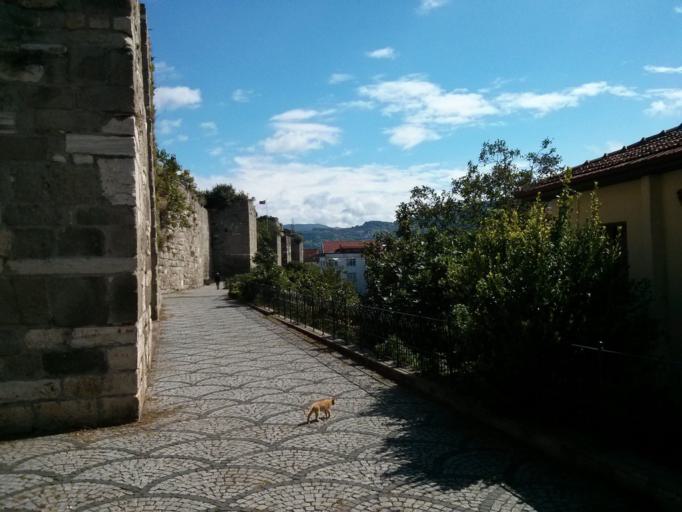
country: TR
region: Bartin
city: Amasra
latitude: 41.7502
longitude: 32.3829
